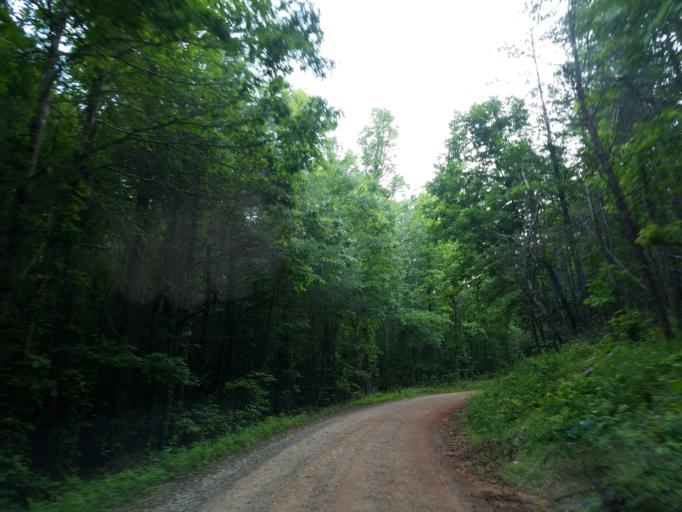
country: US
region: Georgia
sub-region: Lumpkin County
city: Dahlonega
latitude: 34.5871
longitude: -84.1225
